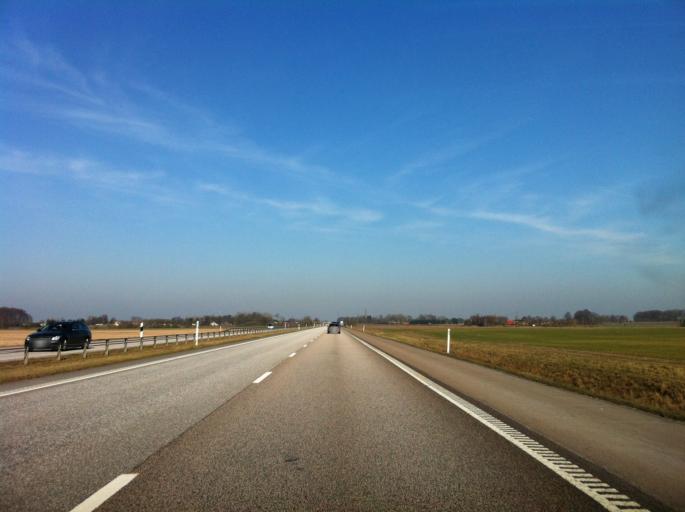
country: SE
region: Skane
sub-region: Angelholms Kommun
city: Strovelstorp
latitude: 56.1642
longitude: 12.8448
